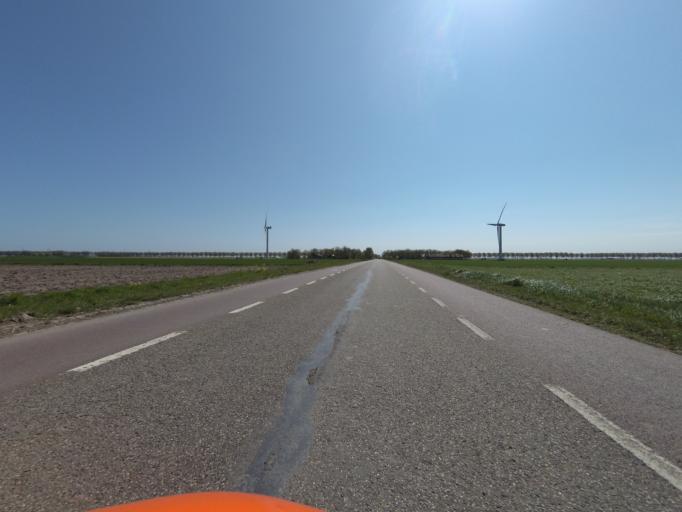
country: NL
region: Flevoland
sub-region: Gemeente Lelystad
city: Lelystad
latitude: 52.3966
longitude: 5.4312
